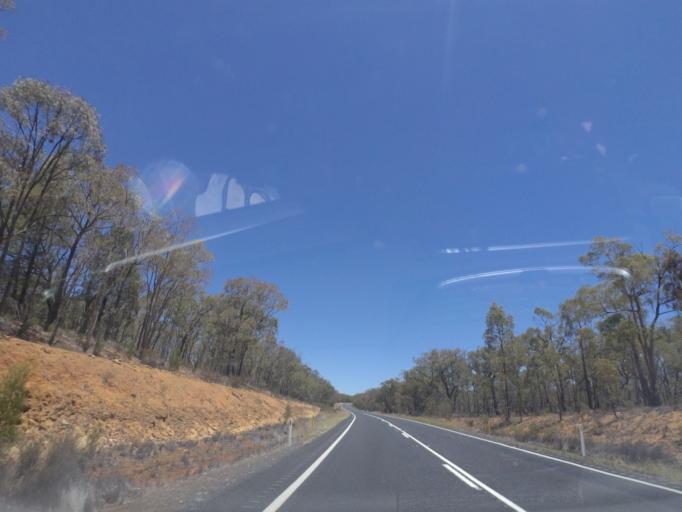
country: AU
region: New South Wales
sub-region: Warrumbungle Shire
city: Coonabarabran
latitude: -31.1818
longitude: 149.3552
